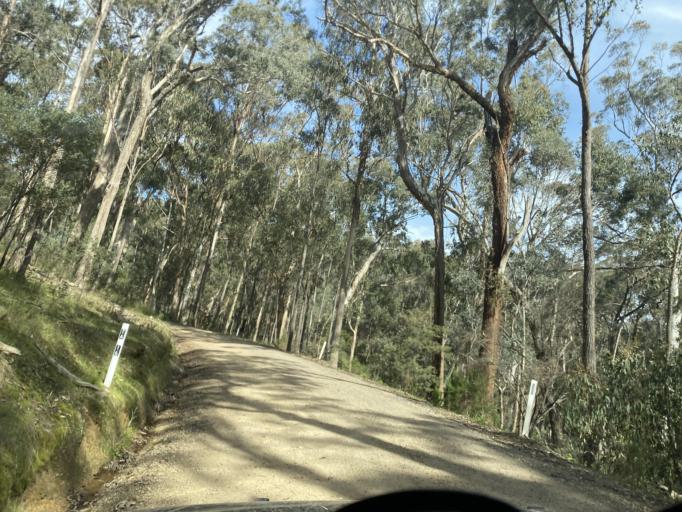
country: AU
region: Victoria
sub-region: Mansfield
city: Mansfield
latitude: -36.8234
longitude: 146.1520
